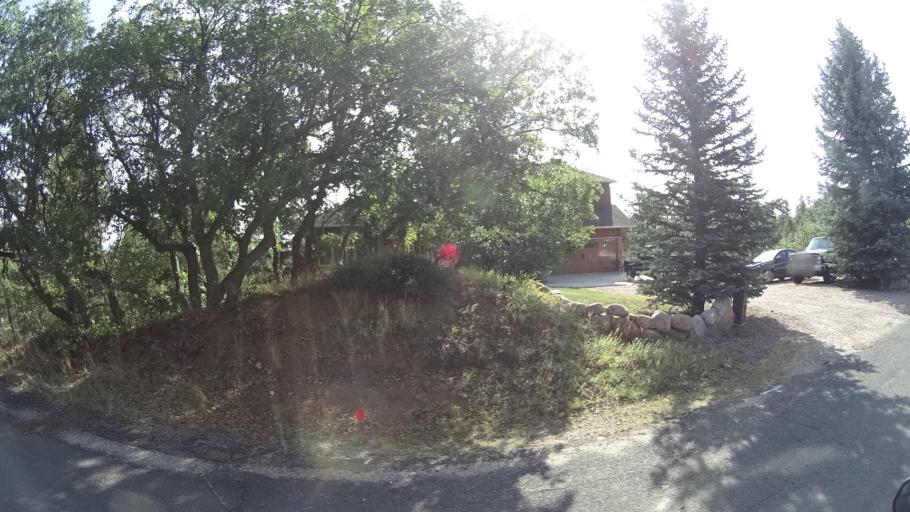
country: US
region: Colorado
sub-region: El Paso County
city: Colorado Springs
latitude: 38.8081
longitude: -104.8733
